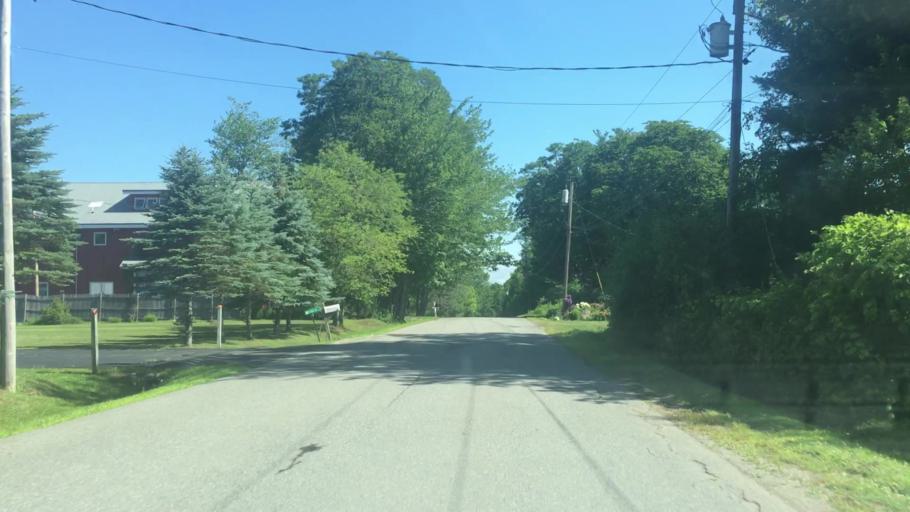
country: US
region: Maine
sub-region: Waldo County
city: Northport
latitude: 44.3783
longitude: -68.9819
